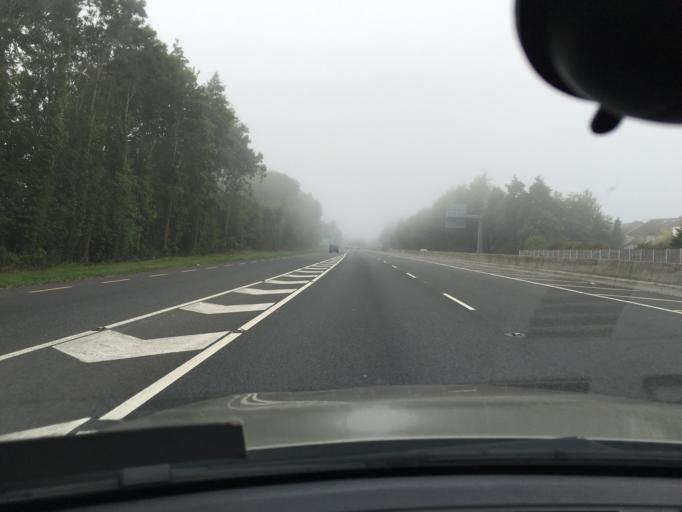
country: IE
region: Leinster
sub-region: An Iarmhi
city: Athlone
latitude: 53.4323
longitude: -7.9278
